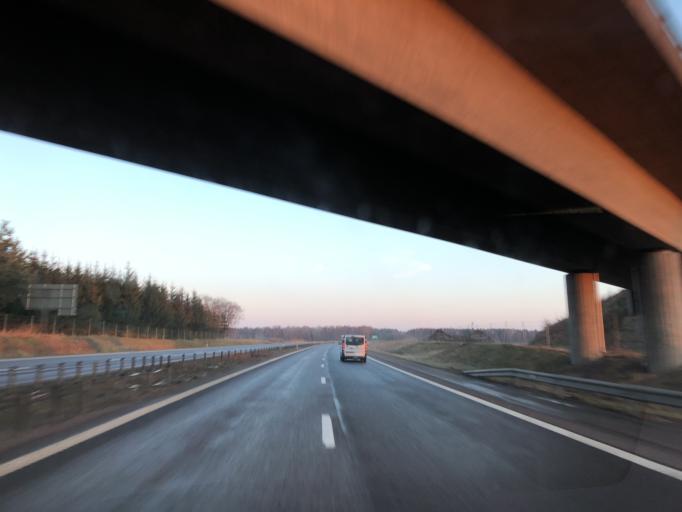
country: SE
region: Halland
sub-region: Laholms Kommun
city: Mellbystrand
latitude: 56.4573
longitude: 12.9447
